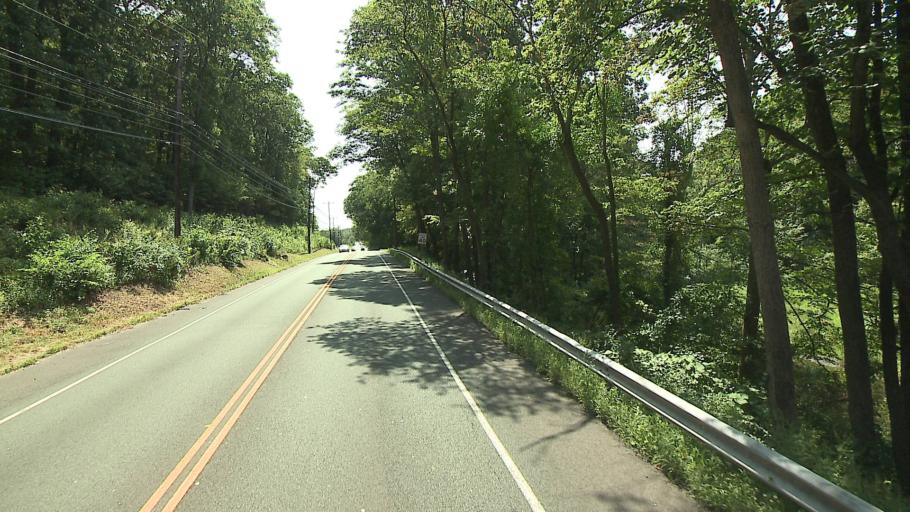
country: US
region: Connecticut
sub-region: Fairfield County
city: Trumbull
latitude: 41.3132
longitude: -73.2593
